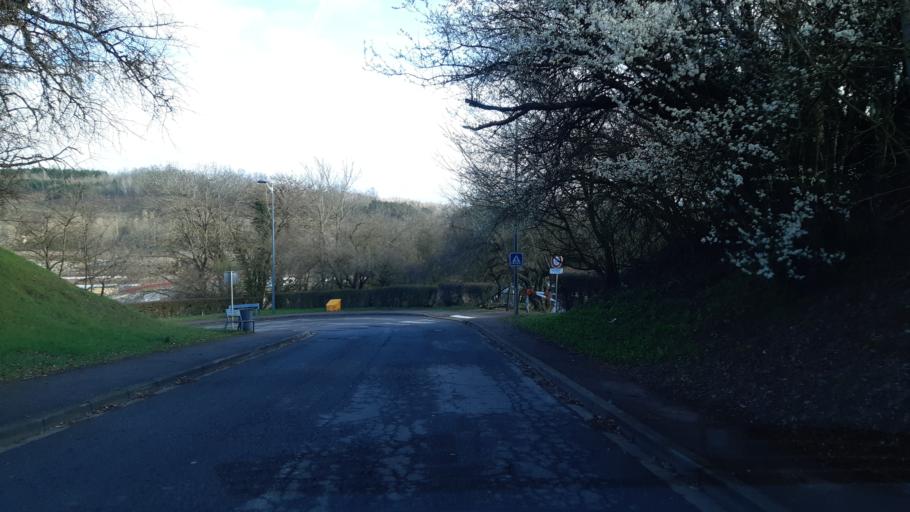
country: FR
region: Lorraine
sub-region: Departement de Meurthe-et-Moselle
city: Villerupt
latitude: 49.4730
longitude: 5.9360
